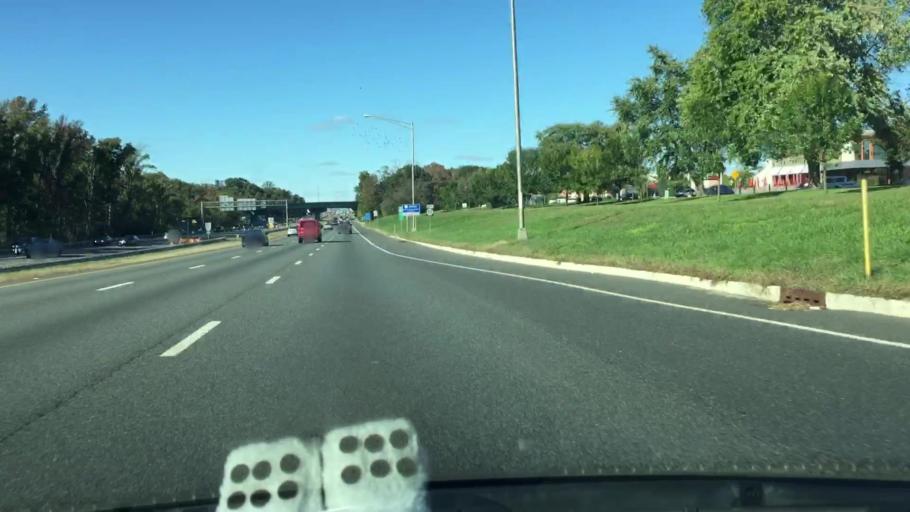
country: US
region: New Jersey
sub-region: Camden County
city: Glendora
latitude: 39.8398
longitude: -75.0926
